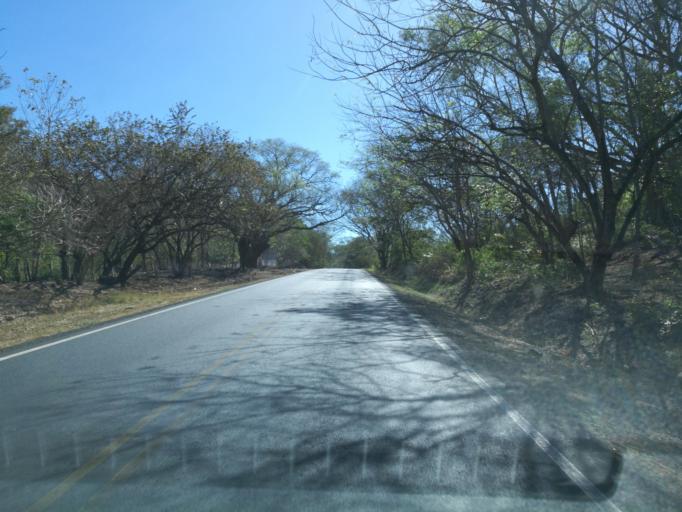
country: CR
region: Puntarenas
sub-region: Canton Central de Puntarenas
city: Puntarenas
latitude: 10.0877
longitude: -84.8439
